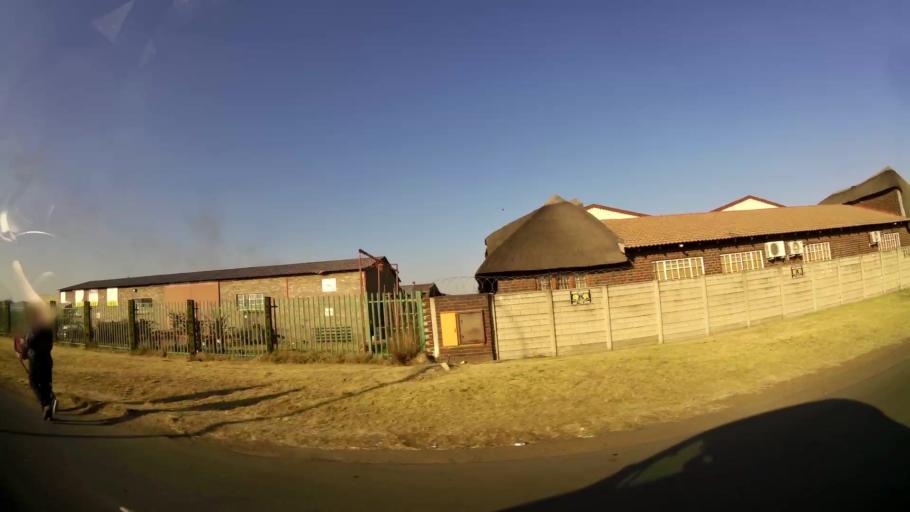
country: ZA
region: Gauteng
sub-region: West Rand District Municipality
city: Randfontein
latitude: -26.1982
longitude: 27.6836
